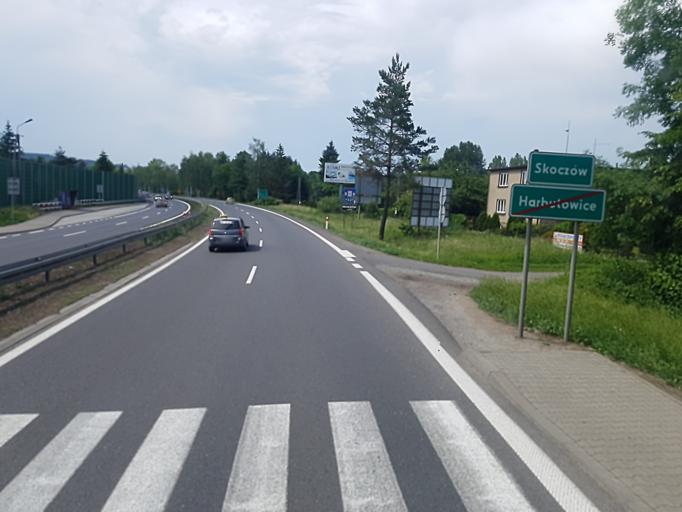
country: PL
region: Silesian Voivodeship
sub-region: Powiat cieszynski
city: Skoczow
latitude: 49.7891
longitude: 18.8024
